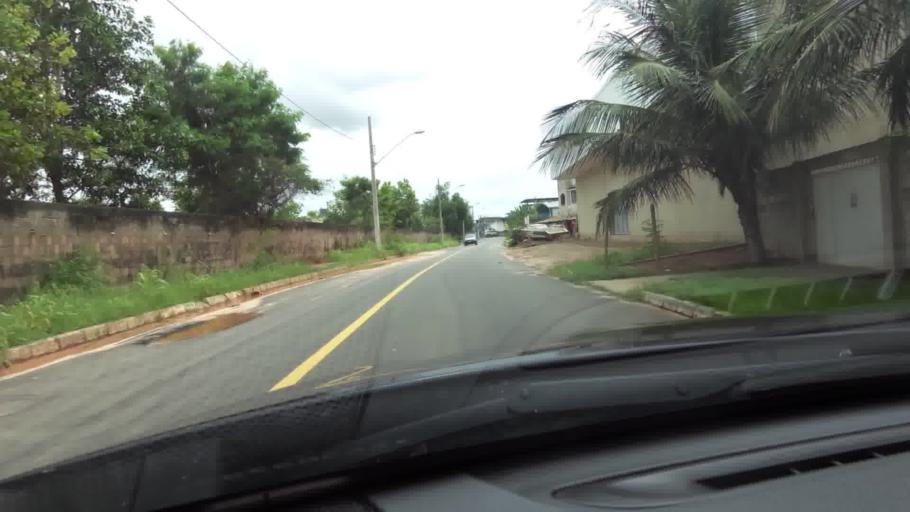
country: BR
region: Espirito Santo
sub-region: Guarapari
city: Guarapari
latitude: -20.6561
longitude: -40.5005
